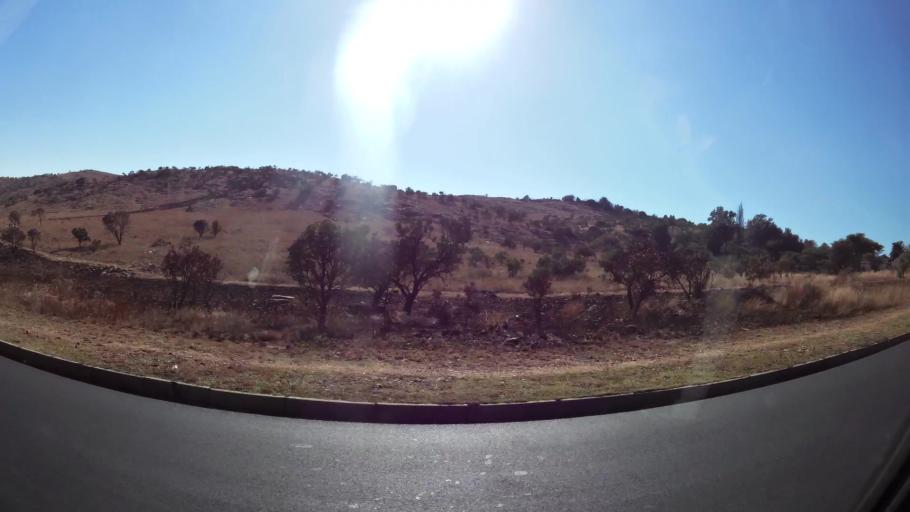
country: ZA
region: Gauteng
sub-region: City of Johannesburg Metropolitan Municipality
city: Roodepoort
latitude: -26.1303
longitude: 27.8862
